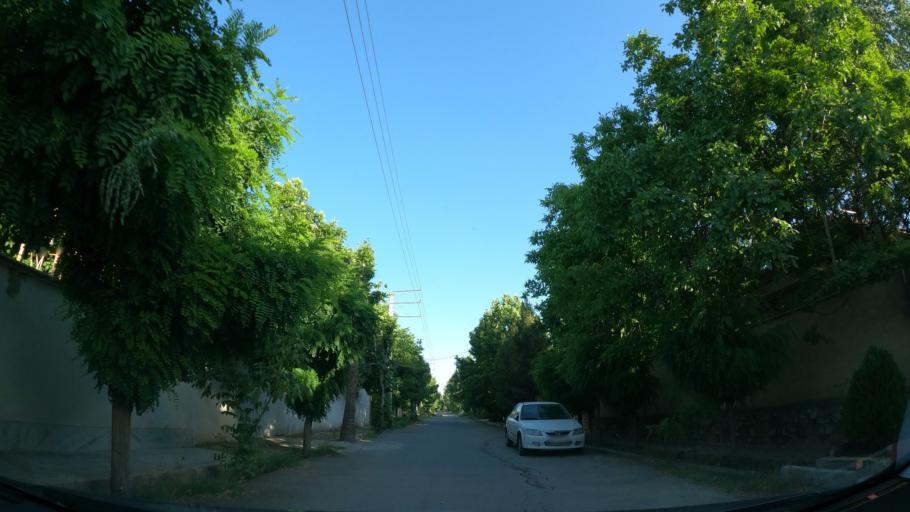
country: IR
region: Alborz
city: Hashtgerd
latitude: 35.9126
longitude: 50.7200
